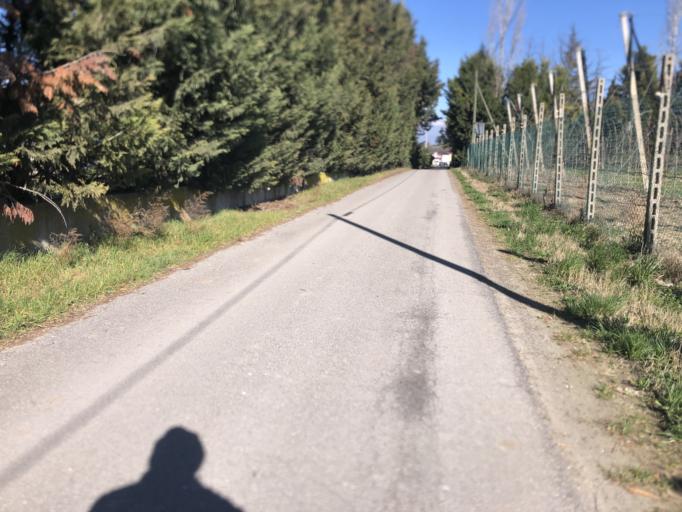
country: IT
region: Veneto
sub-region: Provincia di Verona
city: Sona
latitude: 45.4380
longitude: 10.8157
